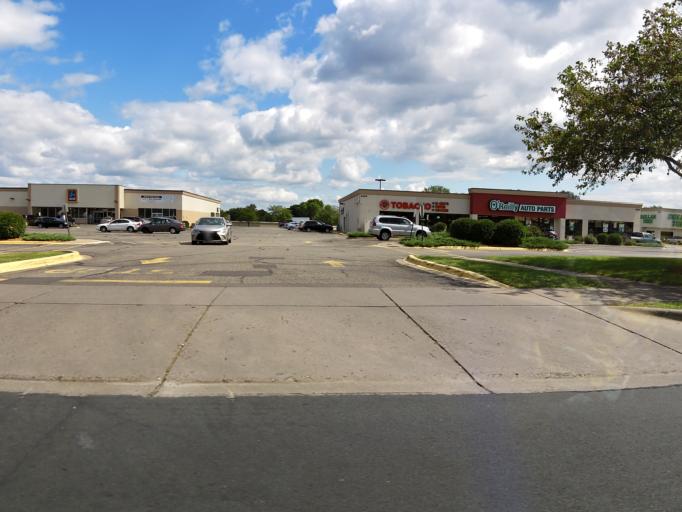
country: US
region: Minnesota
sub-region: Dakota County
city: Inver Grove Heights
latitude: 44.8538
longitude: -93.0449
